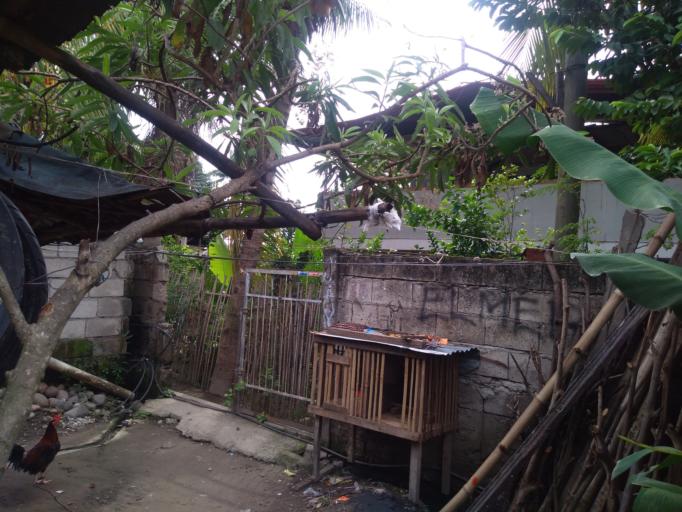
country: PH
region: Central Visayas
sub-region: Province of Negros Oriental
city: Dumaguete
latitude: 9.3033
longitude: 123.2982
